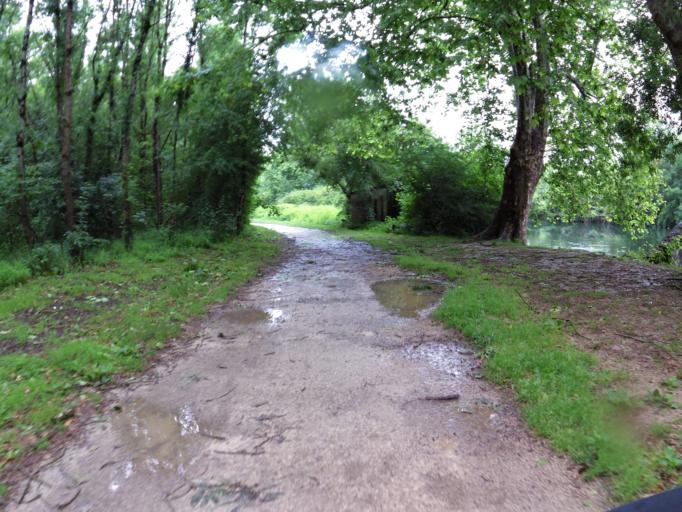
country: FR
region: Poitou-Charentes
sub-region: Departement de la Charente
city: Gond-Pontouvre
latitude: 45.6683
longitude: 0.1567
